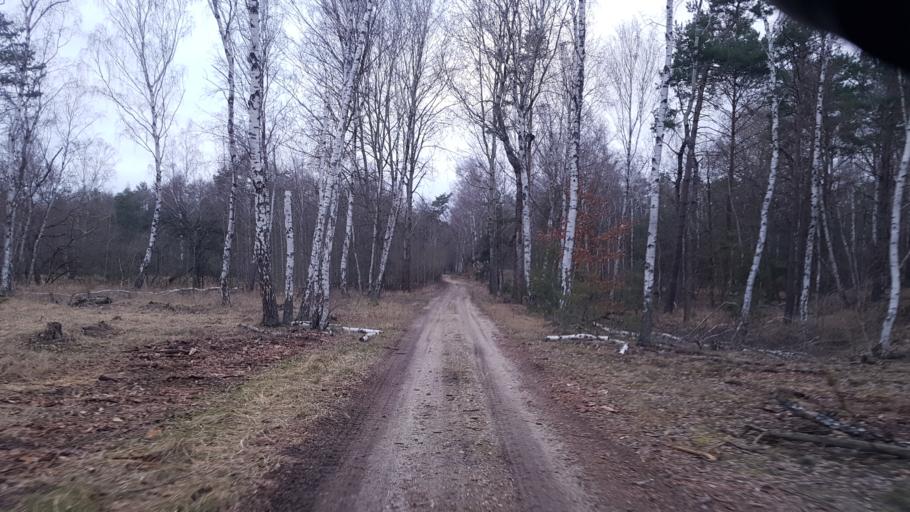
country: DE
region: Brandenburg
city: Trobitz
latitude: 51.6193
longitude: 13.4200
